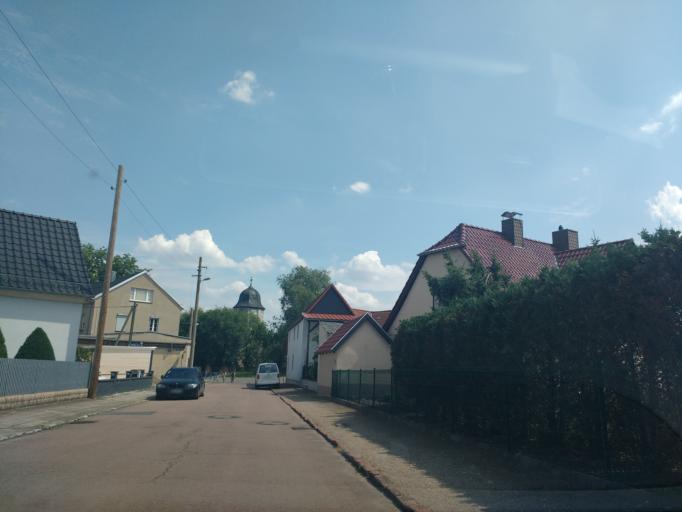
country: DE
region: Saxony-Anhalt
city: Dieskau
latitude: 51.4576
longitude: 12.0359
